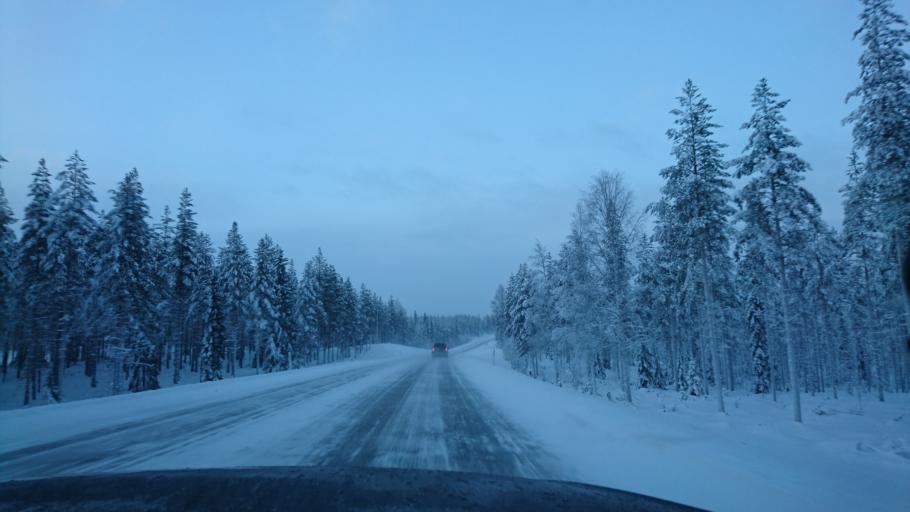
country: FI
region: Northern Ostrobothnia
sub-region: Koillismaa
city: Taivalkoski
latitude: 65.4682
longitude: 27.7166
